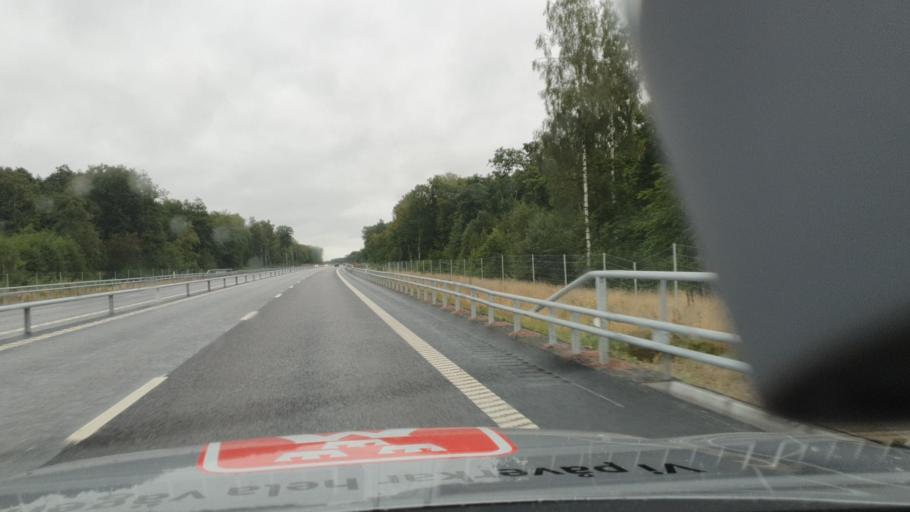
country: SE
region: Skane
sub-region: Kristianstads Kommun
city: Onnestad
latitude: 55.9610
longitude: 13.9613
